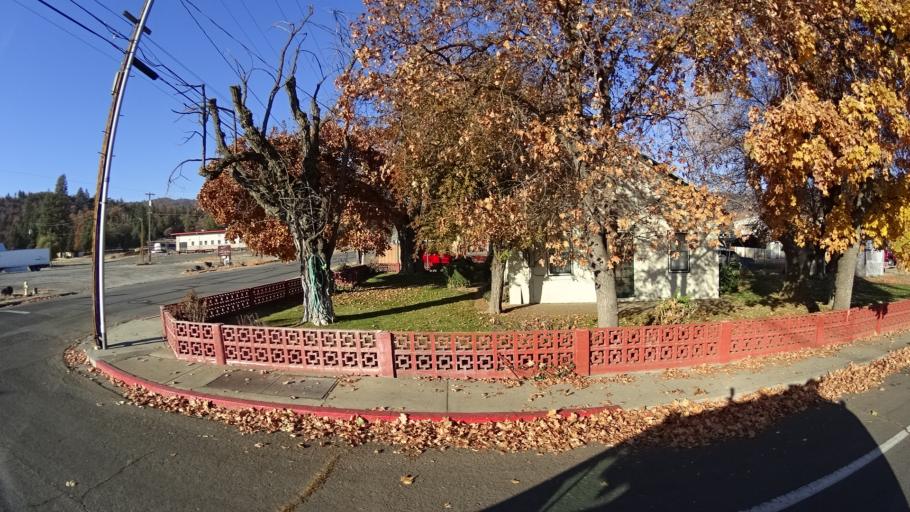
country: US
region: California
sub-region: Siskiyou County
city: Yreka
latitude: 41.7160
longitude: -122.6427
